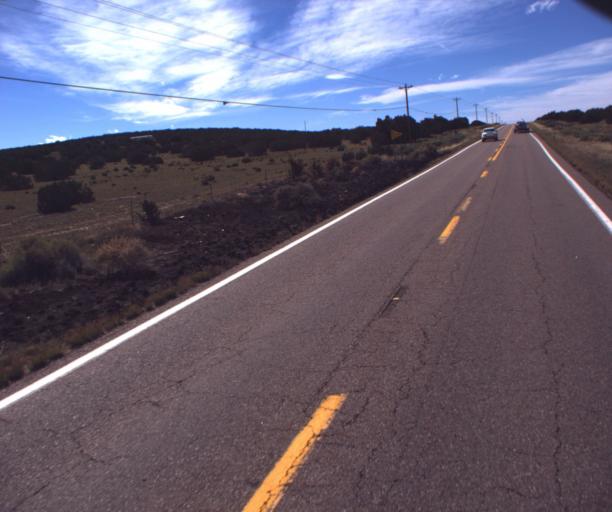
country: US
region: Arizona
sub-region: Apache County
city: Saint Johns
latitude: 34.4854
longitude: -109.5447
